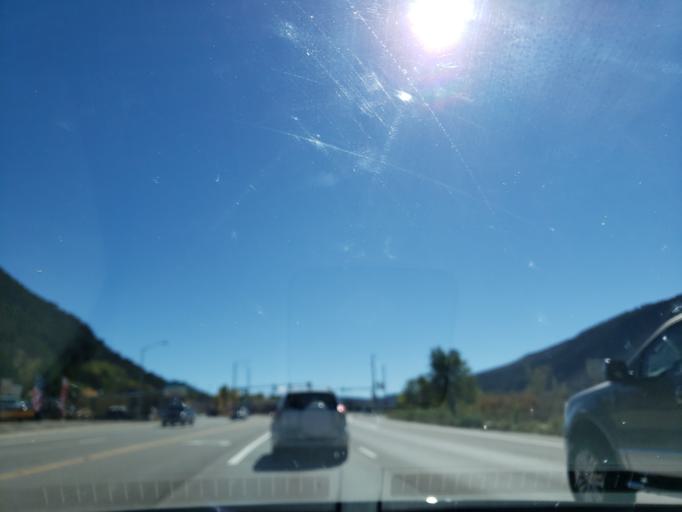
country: US
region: Colorado
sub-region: Garfield County
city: Glenwood Springs
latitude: 39.5265
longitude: -107.3231
